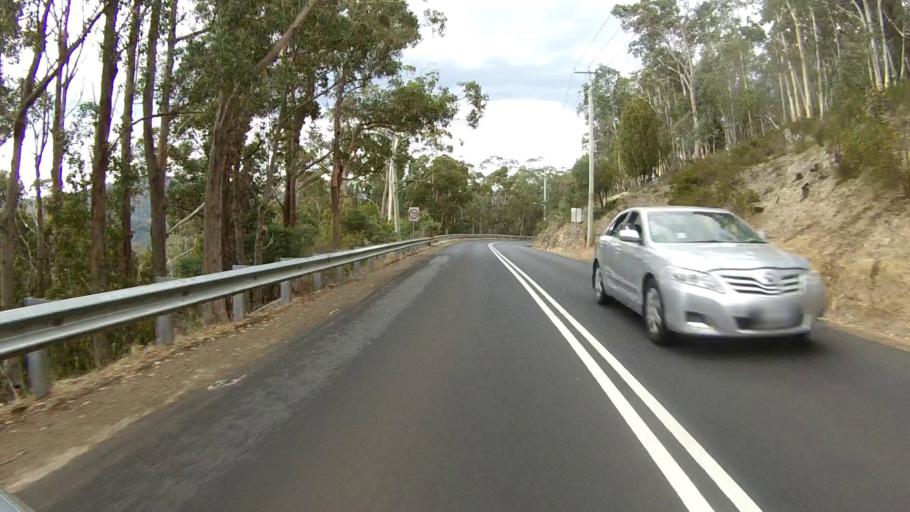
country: AU
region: Tasmania
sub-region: Hobart
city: Dynnyrne
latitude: -42.9055
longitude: 147.2774
